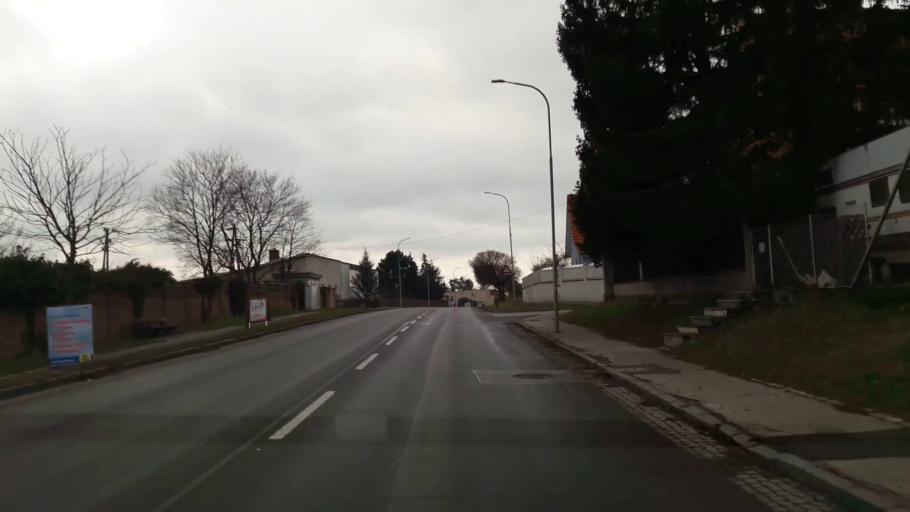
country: AT
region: Lower Austria
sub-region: Politischer Bezirk Wien-Umgebung
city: Lanzendorf
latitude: 48.1031
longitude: 16.4314
